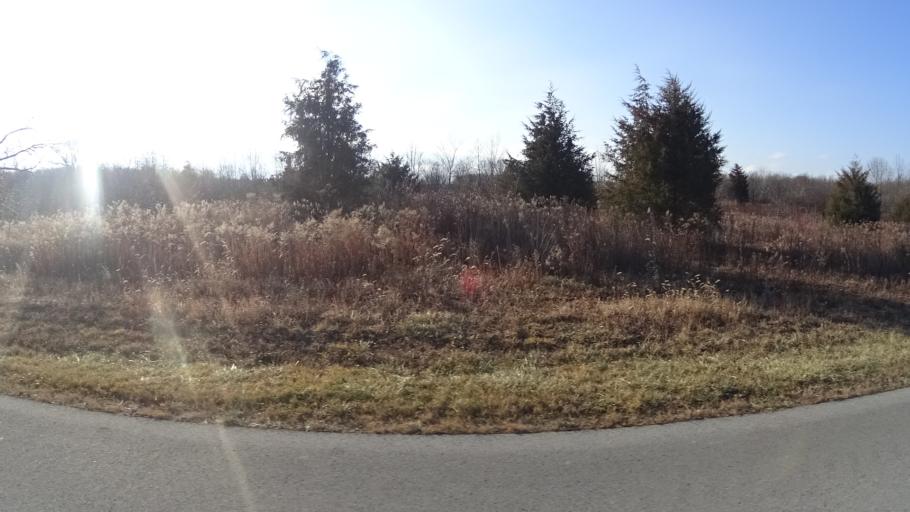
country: US
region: Ohio
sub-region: Lorain County
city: Oberlin
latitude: 41.2506
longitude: -82.2382
